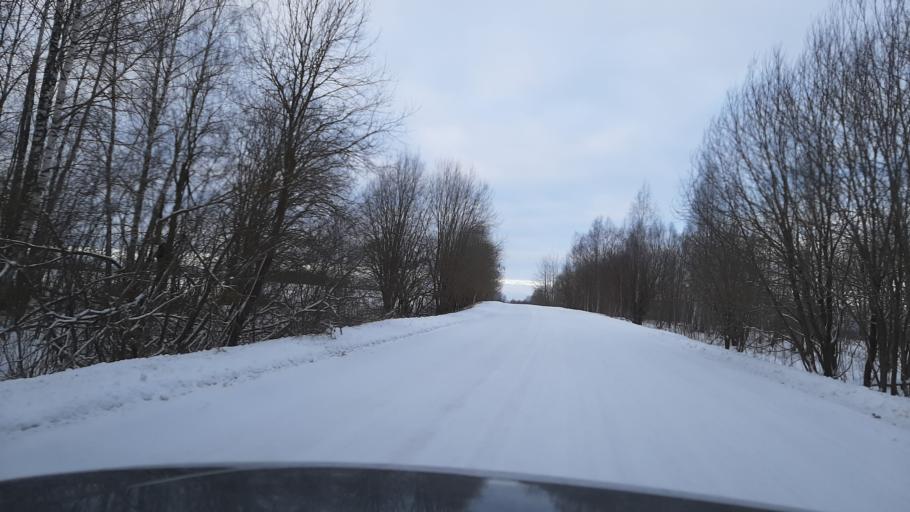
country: RU
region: Kostroma
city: Kosmynino
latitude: 57.4782
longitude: 40.8647
